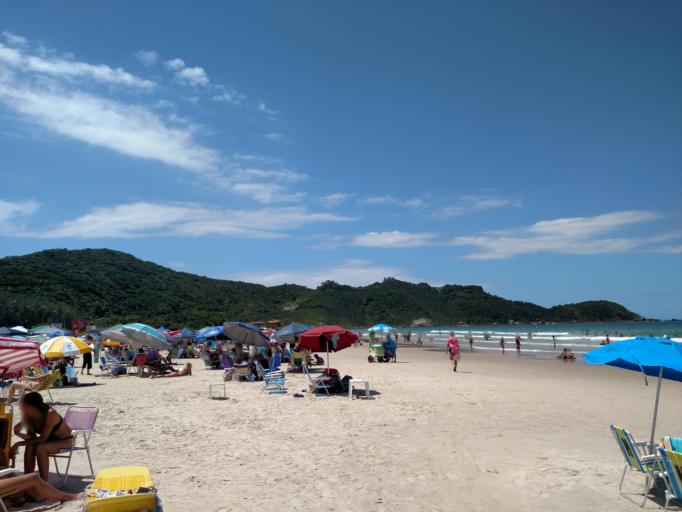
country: BR
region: Santa Catarina
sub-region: Porto Belo
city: Porto Belo
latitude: -27.1710
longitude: -48.4987
